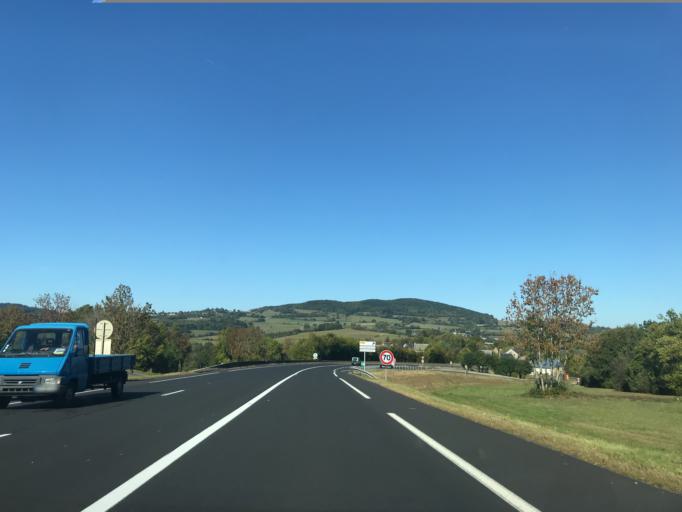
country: FR
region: Auvergne
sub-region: Departement du Puy-de-Dome
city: Gelles
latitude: 45.7212
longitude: 2.8028
